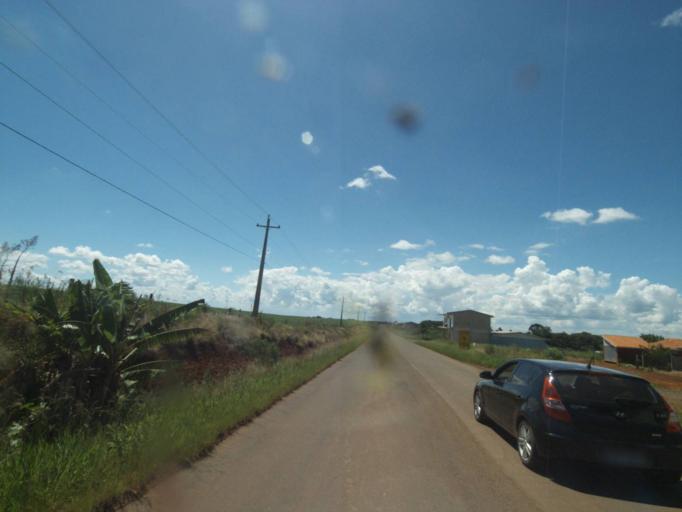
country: BR
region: Parana
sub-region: Pinhao
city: Pinhao
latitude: -25.8315
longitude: -52.0337
